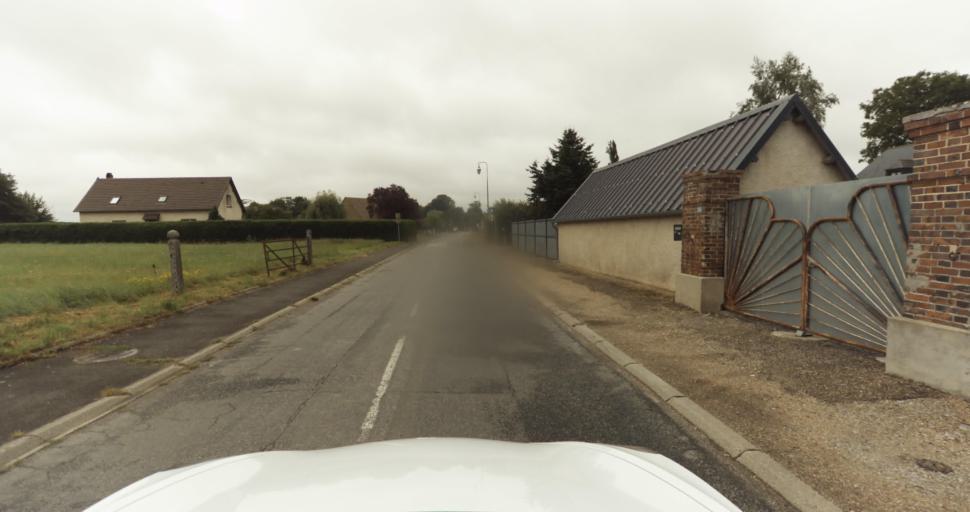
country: FR
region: Haute-Normandie
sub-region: Departement de l'Eure
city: Aviron
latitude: 49.0811
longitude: 1.0702
